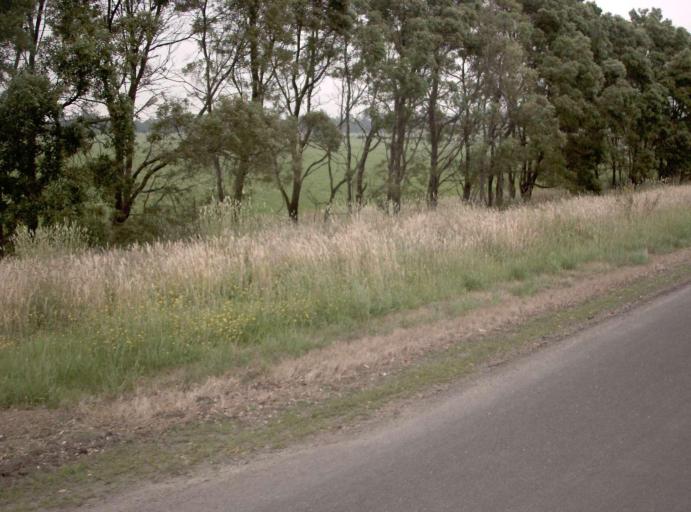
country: AU
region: Victoria
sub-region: Baw Baw
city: Warragul
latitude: -38.1953
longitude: 146.0295
